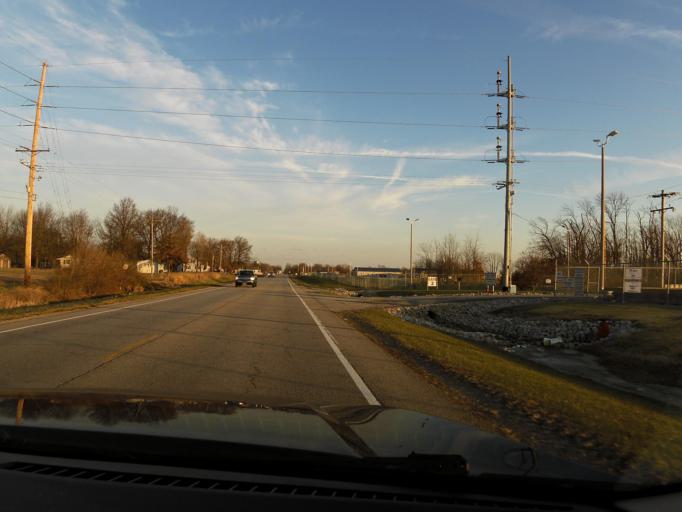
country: US
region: Illinois
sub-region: Fayette County
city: Vandalia
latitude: 38.7936
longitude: -89.0864
